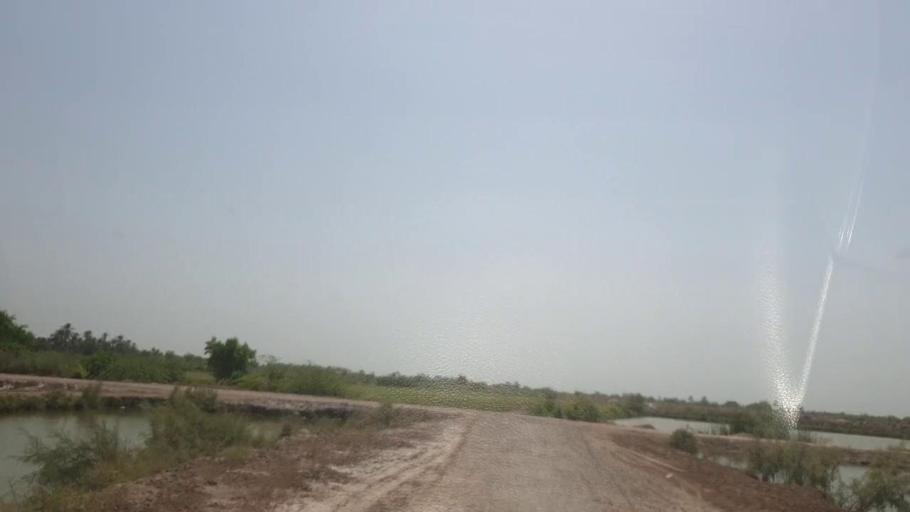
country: PK
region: Sindh
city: Gambat
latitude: 27.3151
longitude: 68.5407
